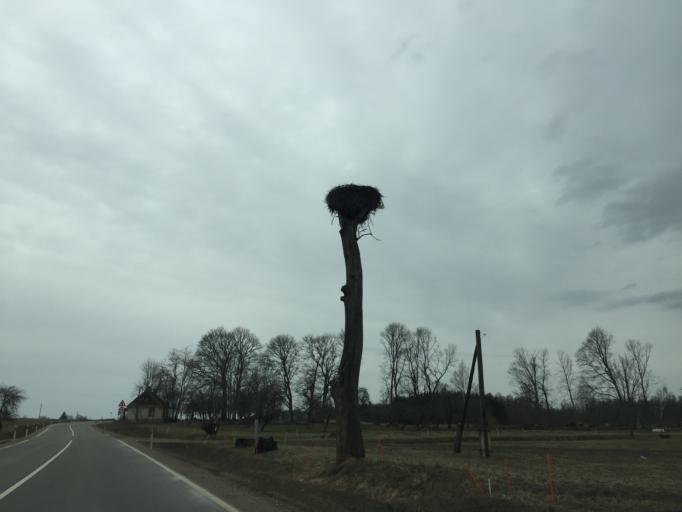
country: LV
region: Ilukste
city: Ilukste
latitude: 56.0002
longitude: 26.2818
